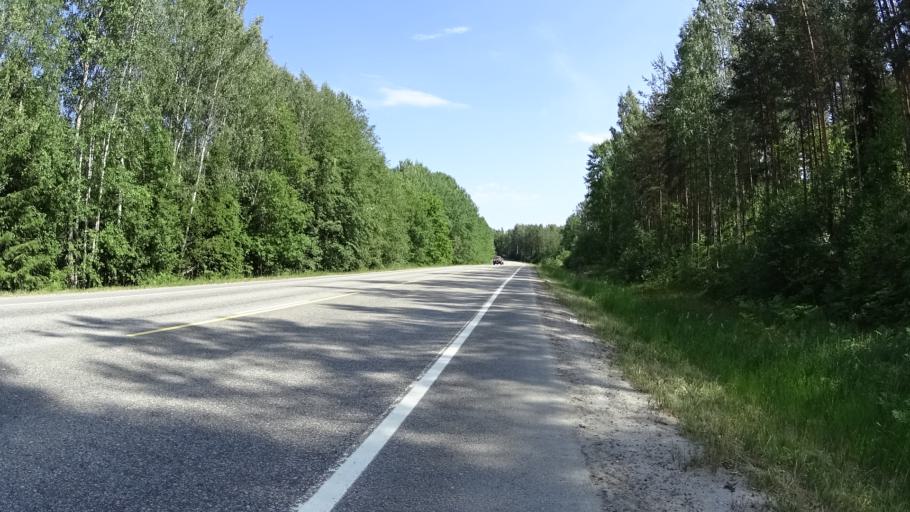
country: FI
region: Uusimaa
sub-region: Raaseporin
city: Karis
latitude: 60.0901
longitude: 23.6436
